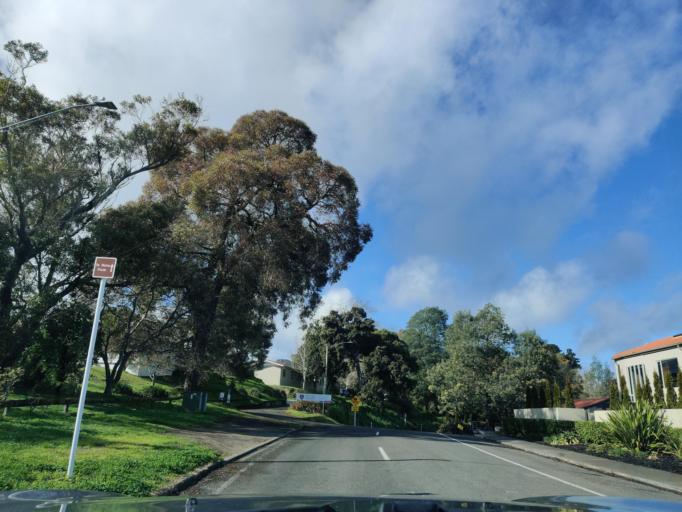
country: NZ
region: Hawke's Bay
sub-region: Hastings District
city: Hastings
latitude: -39.6757
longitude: 176.8956
